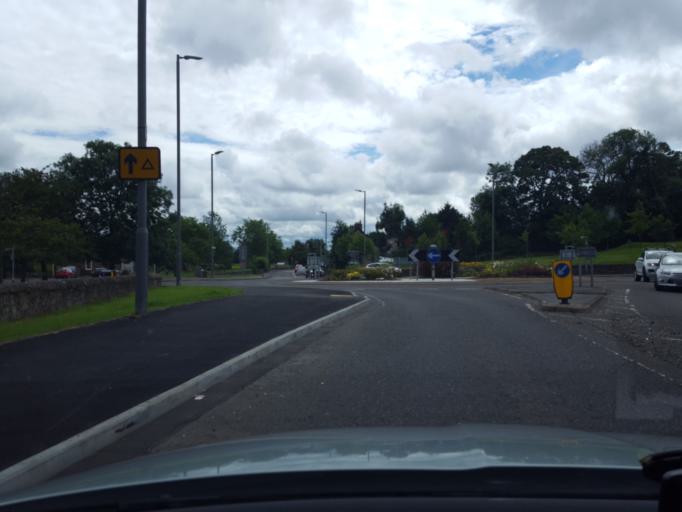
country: GB
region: Scotland
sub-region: Stirling
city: Plean
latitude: 56.0635
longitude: -3.8738
